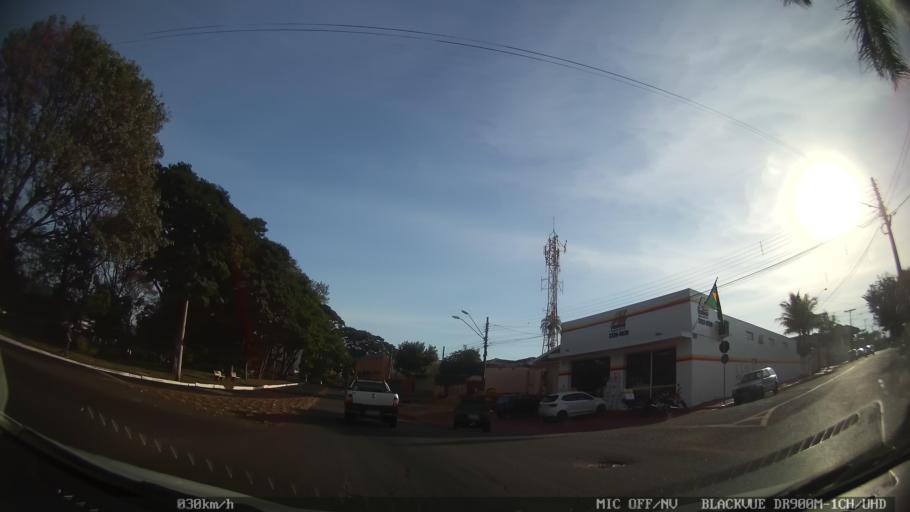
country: BR
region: Sao Paulo
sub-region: Ribeirao Preto
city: Ribeirao Preto
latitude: -21.2674
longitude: -47.8173
